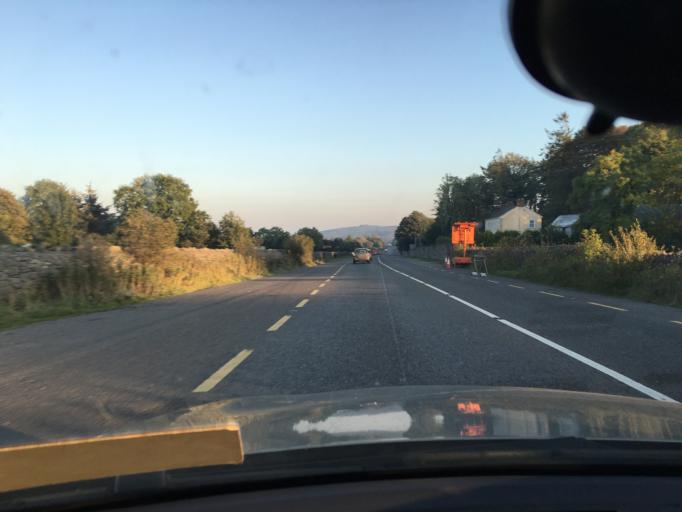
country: IE
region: Connaught
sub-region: County Galway
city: Moycullen
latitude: 53.3208
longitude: -9.1596
